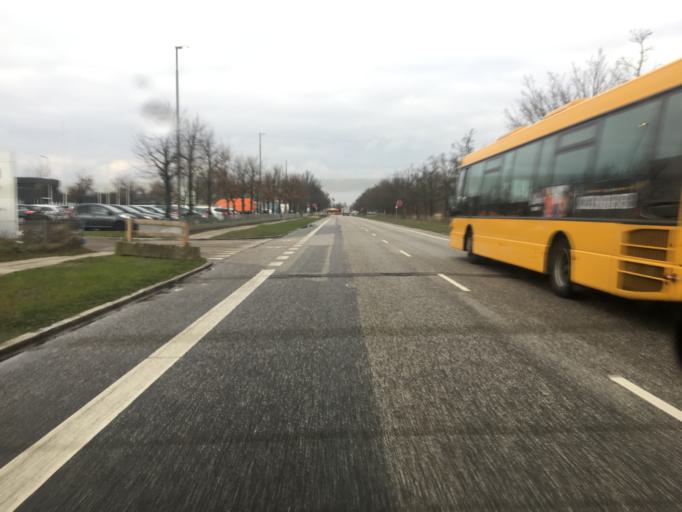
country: DK
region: Capital Region
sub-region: Hvidovre Kommune
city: Hvidovre
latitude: 55.6099
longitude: 12.4899
